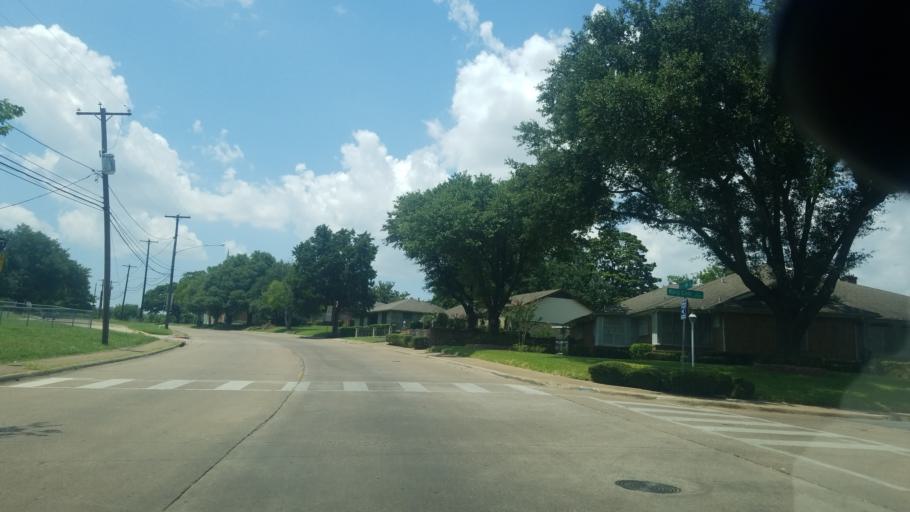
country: US
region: Texas
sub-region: Dallas County
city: Dallas
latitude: 32.7188
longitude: -96.7783
